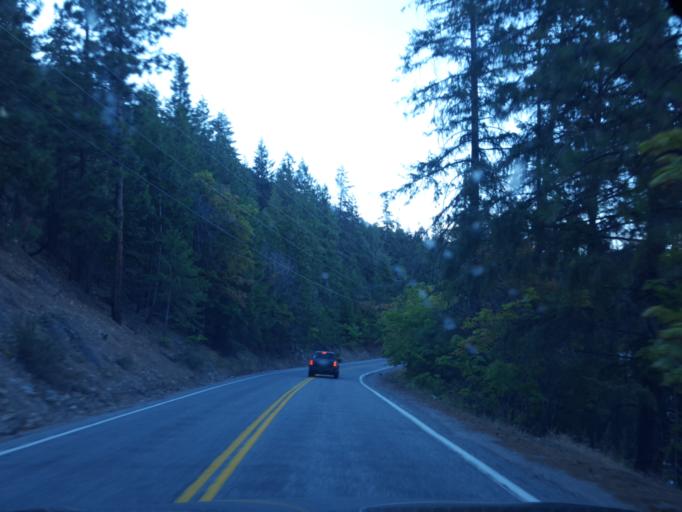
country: US
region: Washington
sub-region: Chelan County
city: Granite Falls
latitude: 47.9071
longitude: -120.2165
